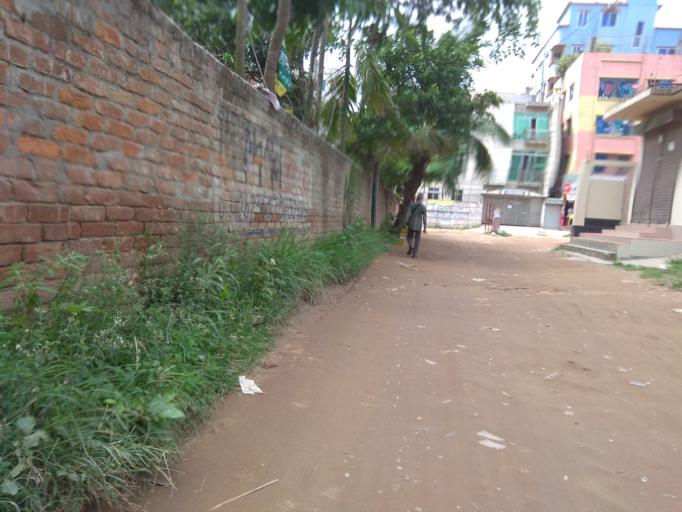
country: BD
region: Dhaka
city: Tungi
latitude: 23.8270
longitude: 90.3527
